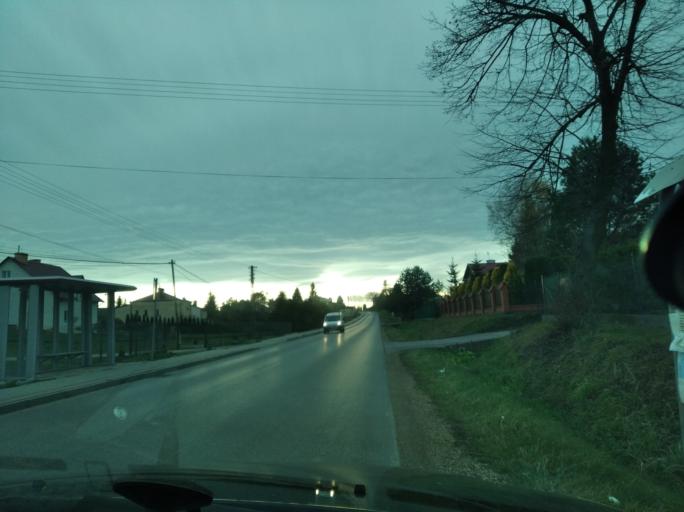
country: PL
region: Subcarpathian Voivodeship
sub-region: Powiat rzeszowski
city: Niechobrz
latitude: 50.0308
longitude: 21.8903
